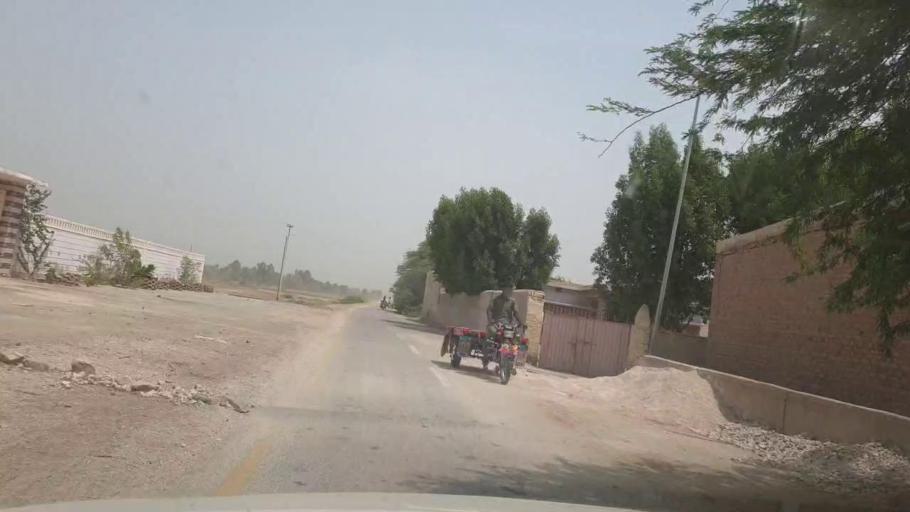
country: PK
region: Sindh
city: Kot Diji
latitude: 27.3943
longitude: 68.6606
